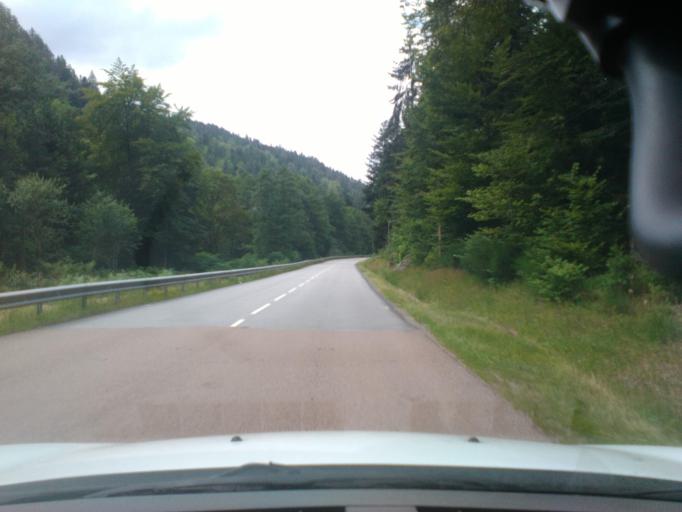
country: FR
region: Lorraine
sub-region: Departement des Vosges
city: Gerardmer
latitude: 48.1032
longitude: 6.8698
